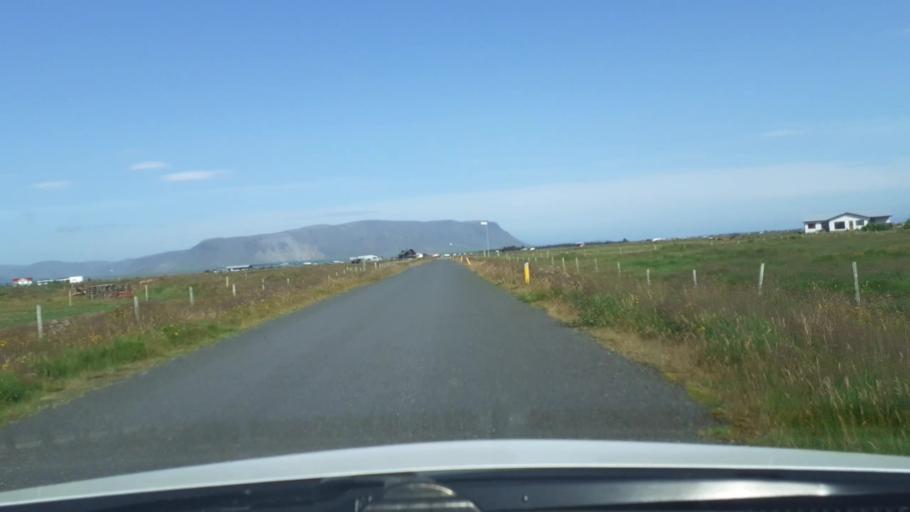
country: IS
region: South
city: Selfoss
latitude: 63.8939
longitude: -21.0825
